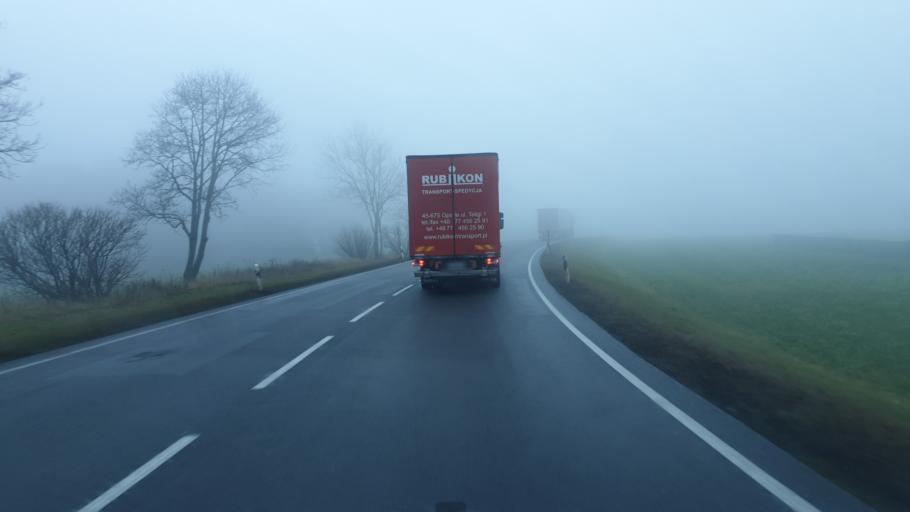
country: DE
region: Saxony
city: Grossolbersdorf
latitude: 50.6885
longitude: 13.1163
